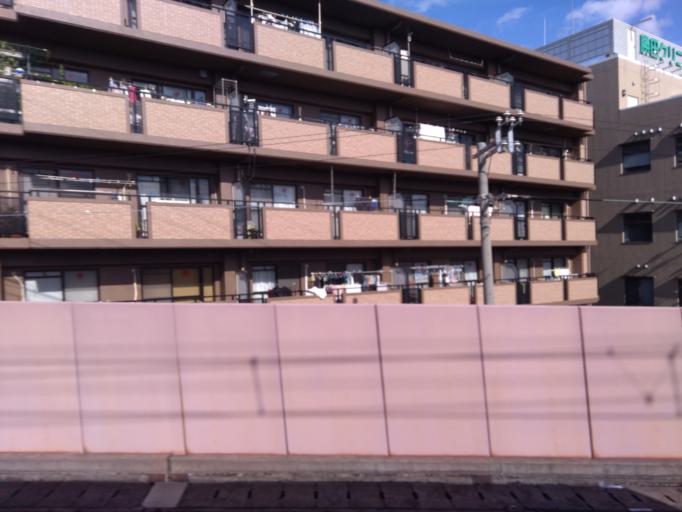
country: JP
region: Osaka
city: Ikeda
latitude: 34.8104
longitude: 135.4431
